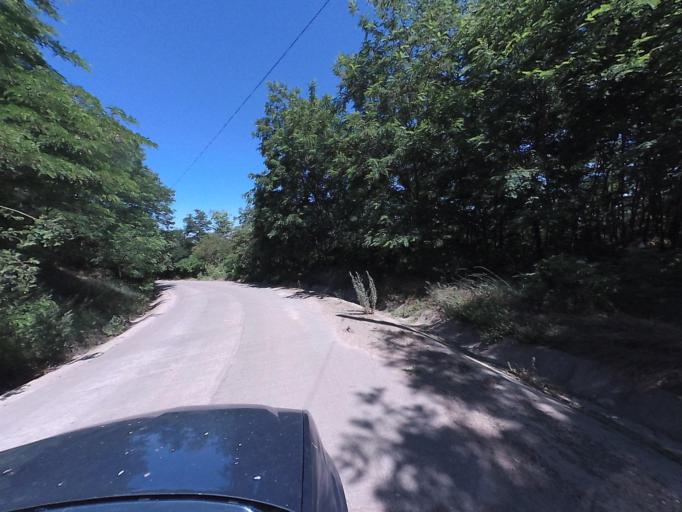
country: RO
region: Vaslui
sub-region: Comuna Costesti
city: Costesti
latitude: 46.4869
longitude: 27.7688
